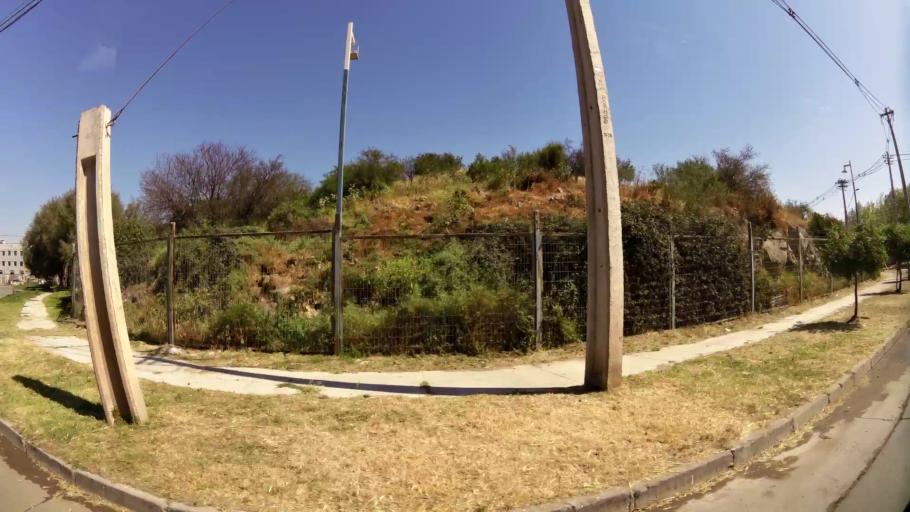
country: CL
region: Santiago Metropolitan
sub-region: Provincia de Santiago
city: Lo Prado
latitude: -33.3850
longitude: -70.7489
